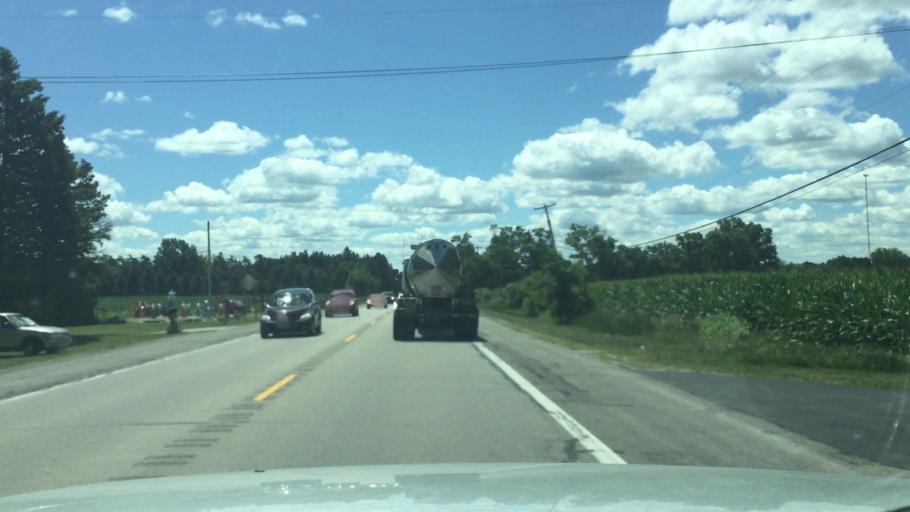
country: US
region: Michigan
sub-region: Saginaw County
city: Shields
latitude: 43.4129
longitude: -84.1309
